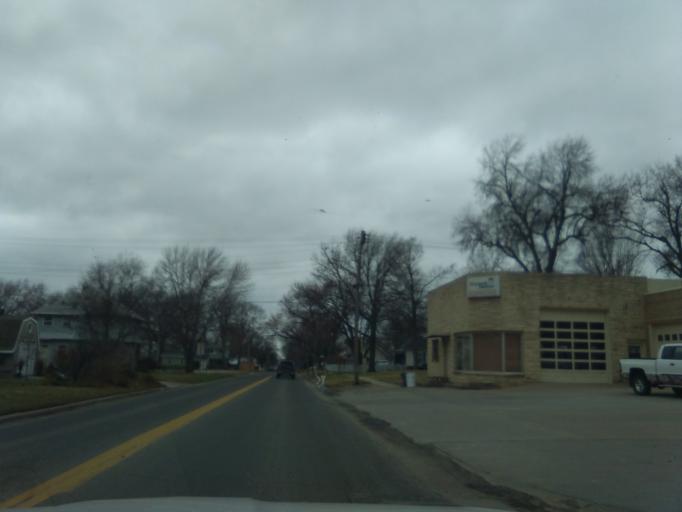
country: US
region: Nebraska
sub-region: Richardson County
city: Falls City
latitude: 40.0657
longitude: -95.6030
